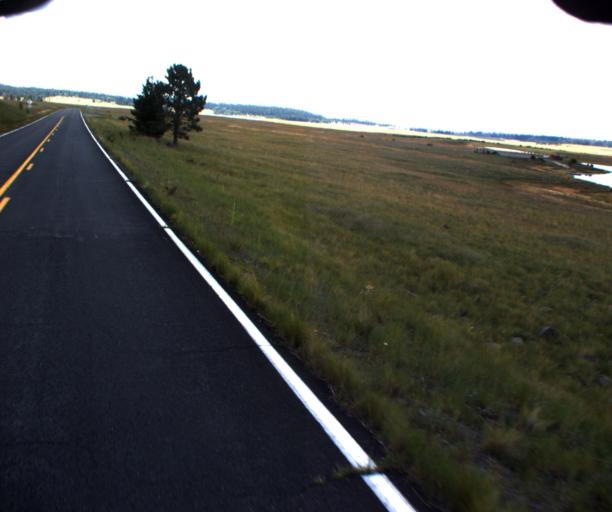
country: US
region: Arizona
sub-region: Apache County
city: Eagar
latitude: 33.9046
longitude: -109.4149
